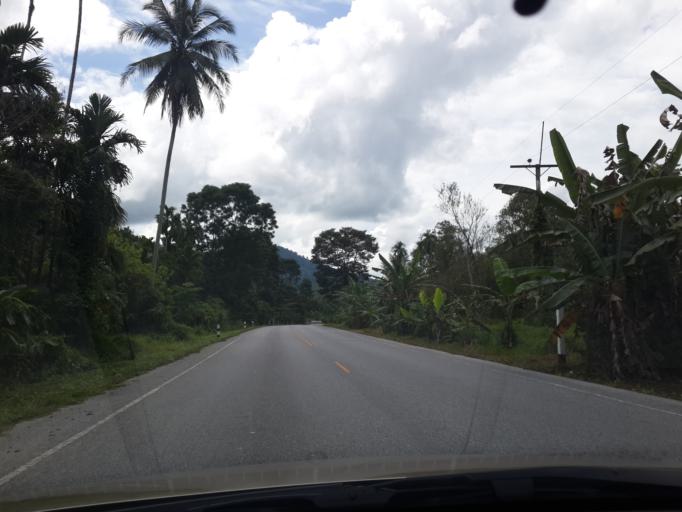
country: TH
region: Yala
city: Raman
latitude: 6.3822
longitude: 101.4006
